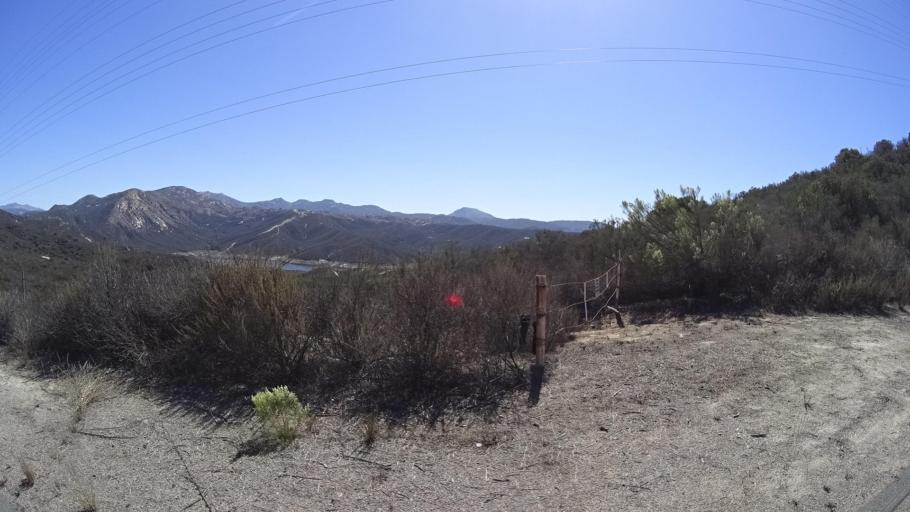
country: US
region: California
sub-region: San Diego County
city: Alpine
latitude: 32.7980
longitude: -116.7784
